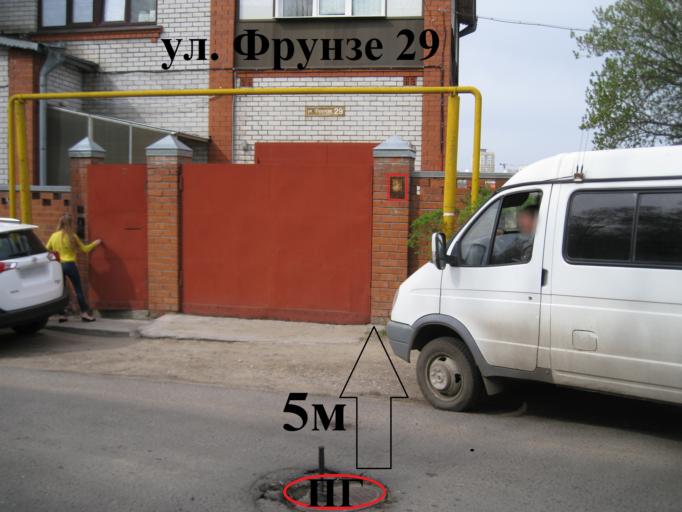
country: RU
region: Voronezj
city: Voronezh
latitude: 51.6565
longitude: 39.2040
